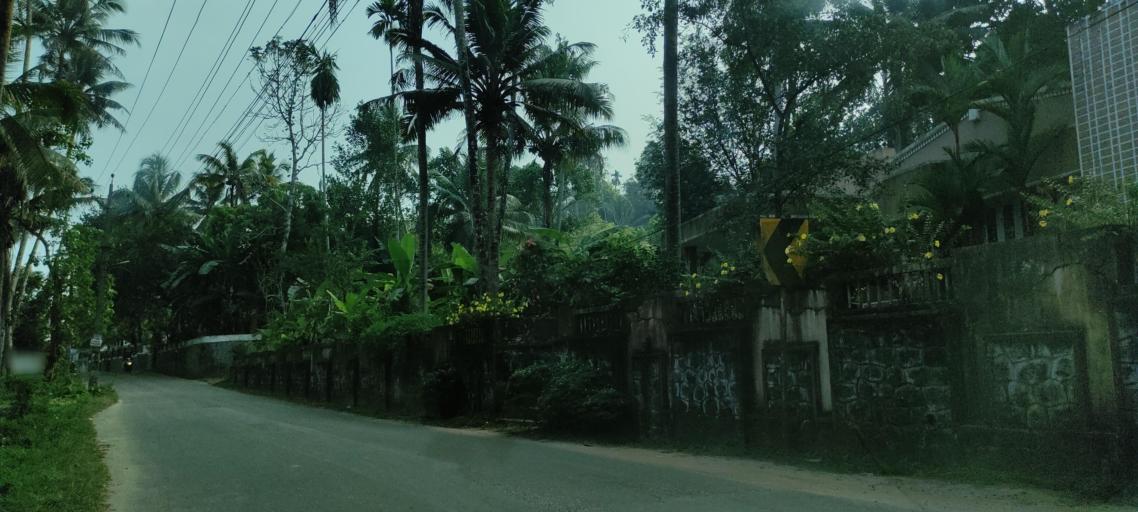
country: IN
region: Kerala
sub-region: Ernakulam
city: Piravam
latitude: 9.7743
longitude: 76.4922
